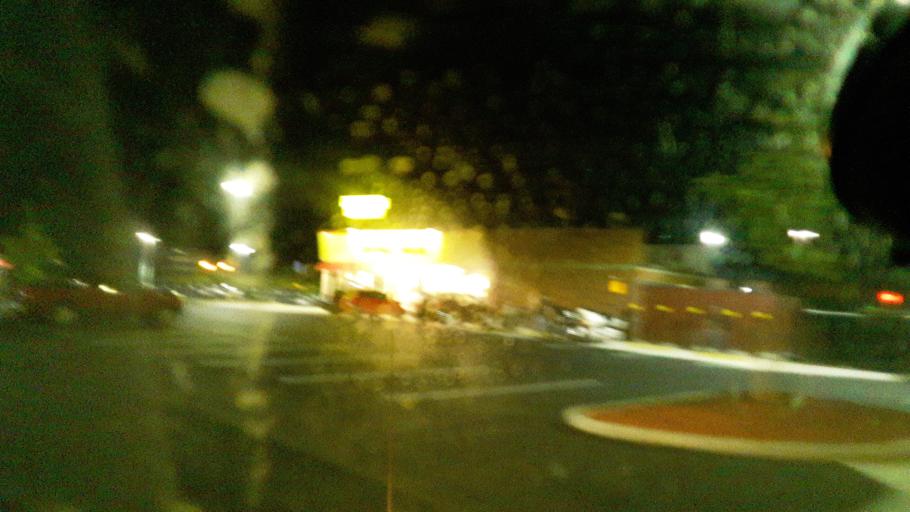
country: US
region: Virginia
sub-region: Wythe County
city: Wytheville
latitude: 36.9506
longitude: -81.0656
